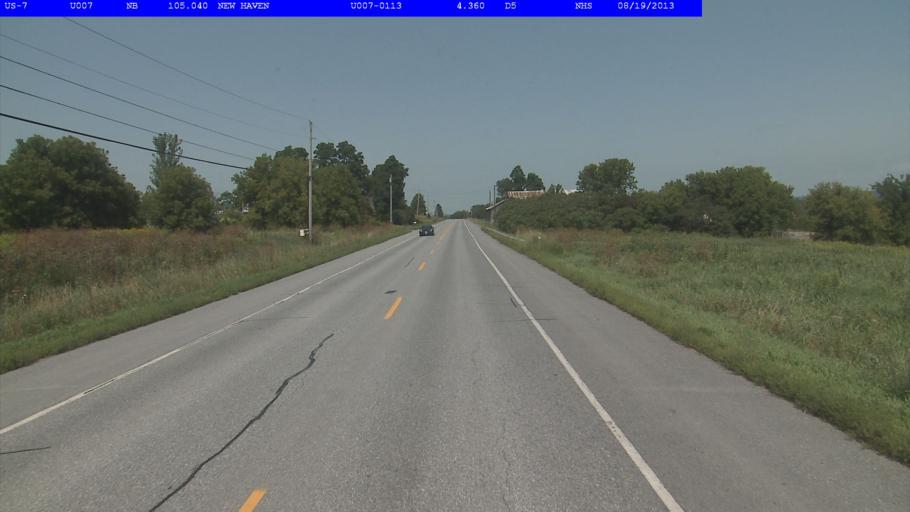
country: US
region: Vermont
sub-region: Addison County
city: Middlebury (village)
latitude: 44.1082
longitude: -73.1745
